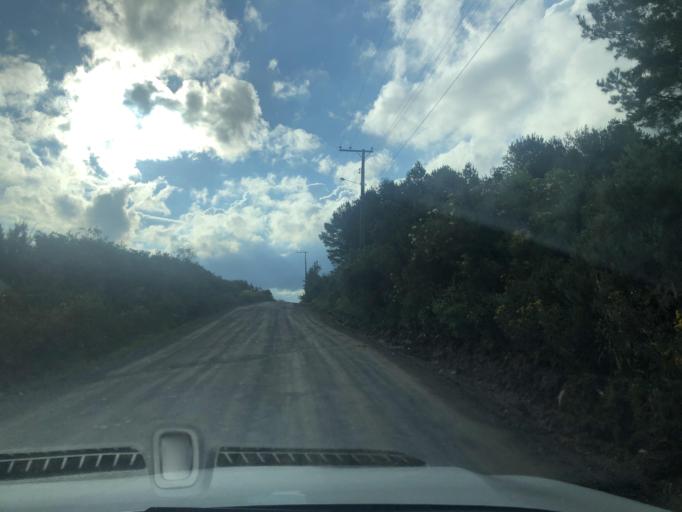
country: BR
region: Santa Catarina
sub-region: Lages
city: Lages
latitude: -27.7917
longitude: -50.3192
